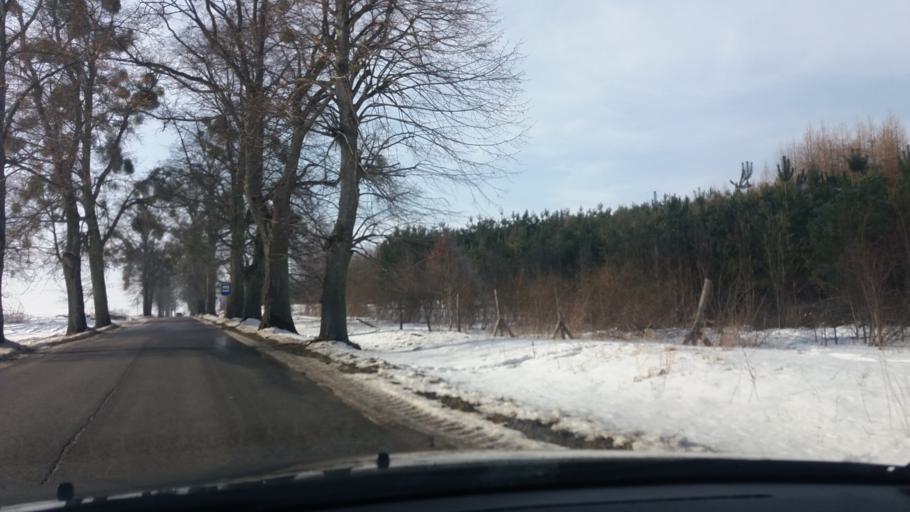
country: PL
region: Warmian-Masurian Voivodeship
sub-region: Powiat lidzbarski
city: Lidzbark Warminski
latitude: 54.1078
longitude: 20.6758
